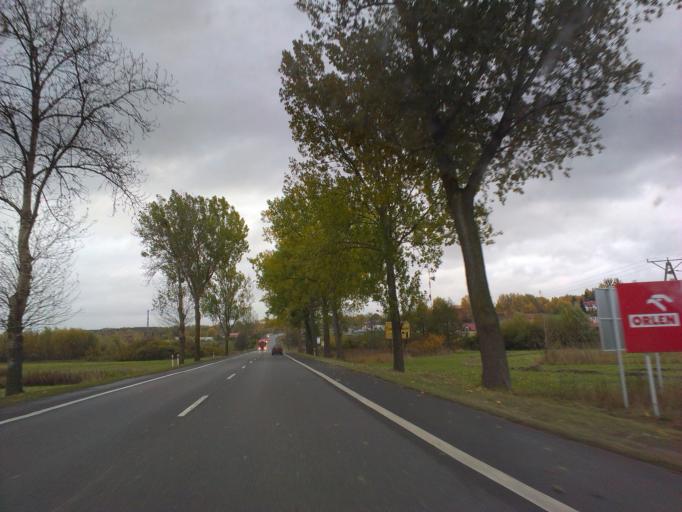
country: PL
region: Kujawsko-Pomorskie
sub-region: Powiat chelminski
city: Chelmno
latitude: 53.3568
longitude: 18.4440
